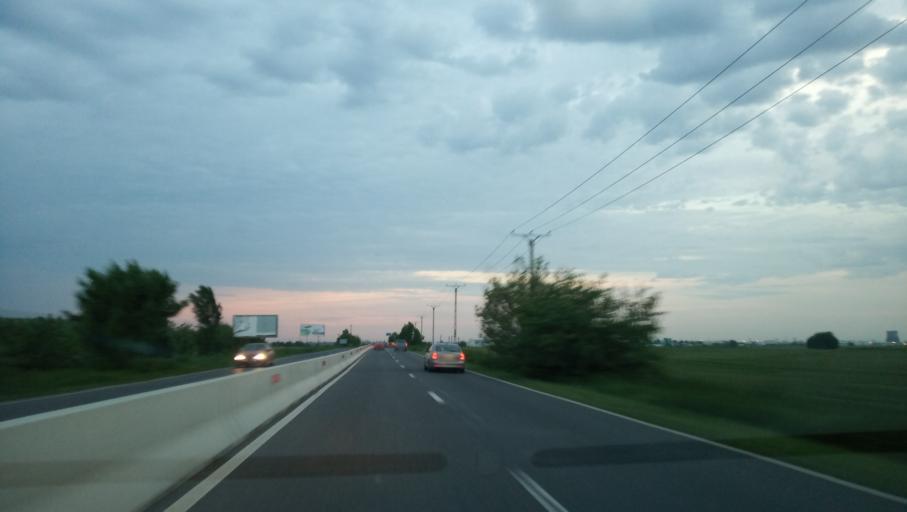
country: RO
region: Timis
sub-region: Comuna Sag
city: Sag
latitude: 45.6779
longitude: 21.1698
